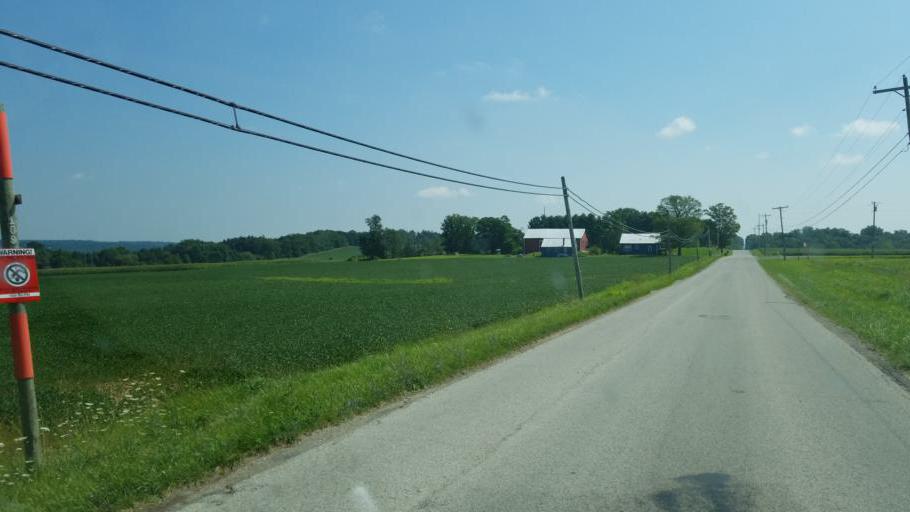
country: US
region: Ohio
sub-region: Richland County
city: Lexington
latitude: 40.6807
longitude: -82.6313
